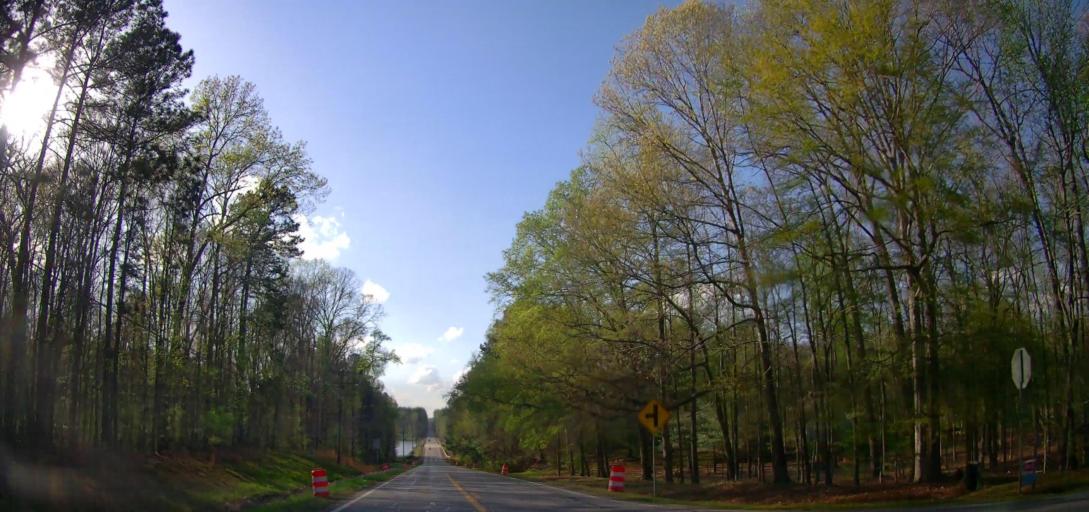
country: US
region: Georgia
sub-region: Baldwin County
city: Milledgeville
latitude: 33.1614
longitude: -83.3710
